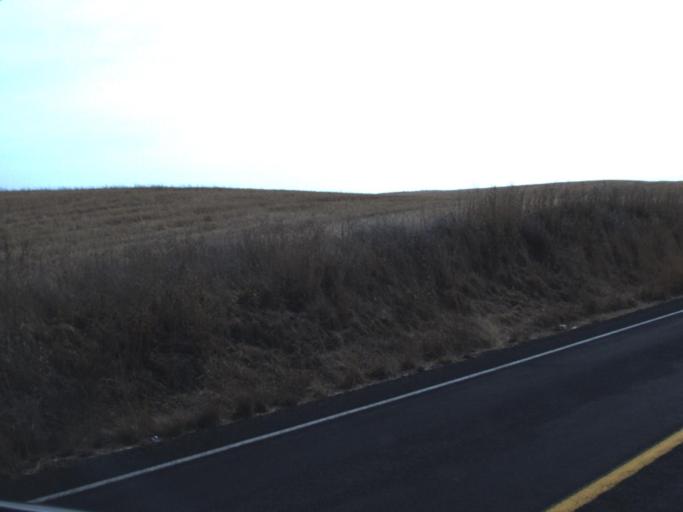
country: US
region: Washington
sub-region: Whitman County
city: Colfax
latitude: 47.0475
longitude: -117.1596
